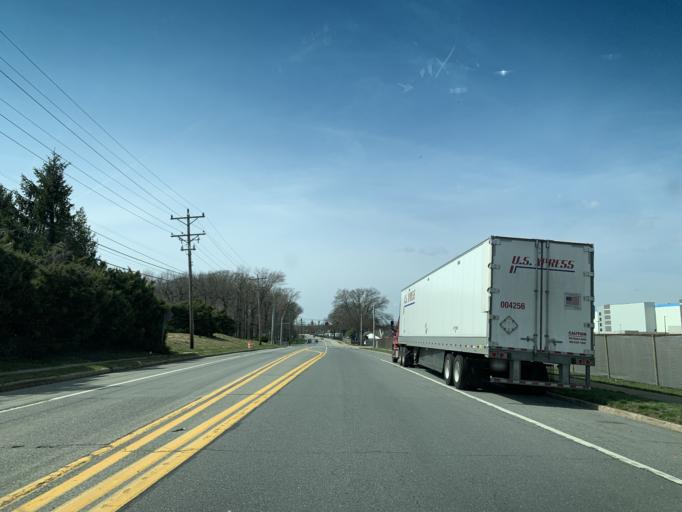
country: US
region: Delaware
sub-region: New Castle County
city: Newport
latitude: 39.7250
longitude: -75.6088
